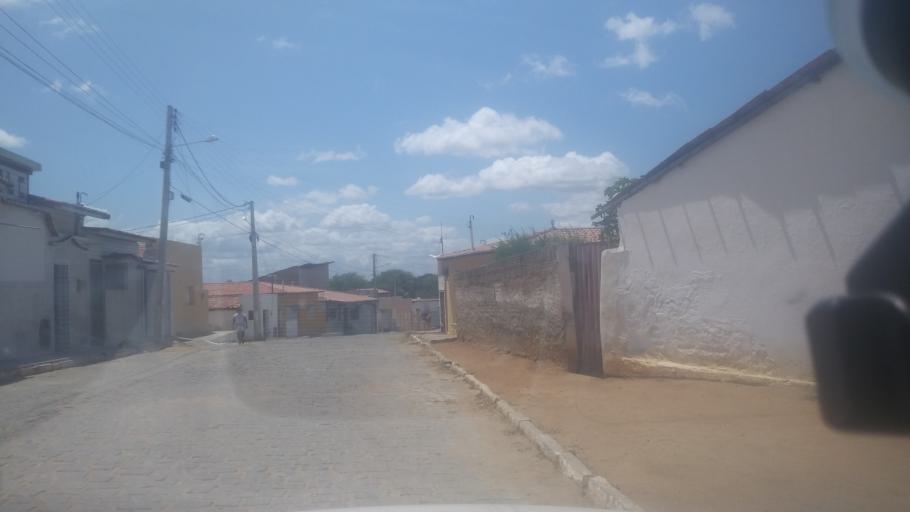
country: BR
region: Rio Grande do Norte
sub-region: Cerro Cora
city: Monte Alegre
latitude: -5.7023
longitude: -36.2472
